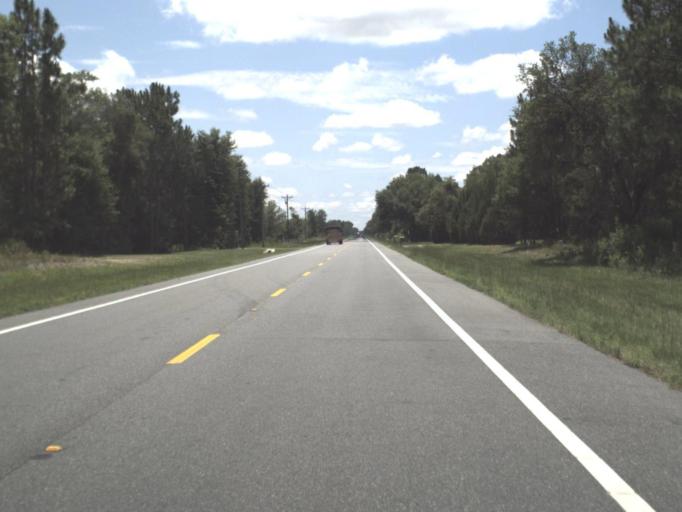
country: US
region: Florida
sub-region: Lafayette County
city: Mayo
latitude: 29.9216
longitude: -82.9508
